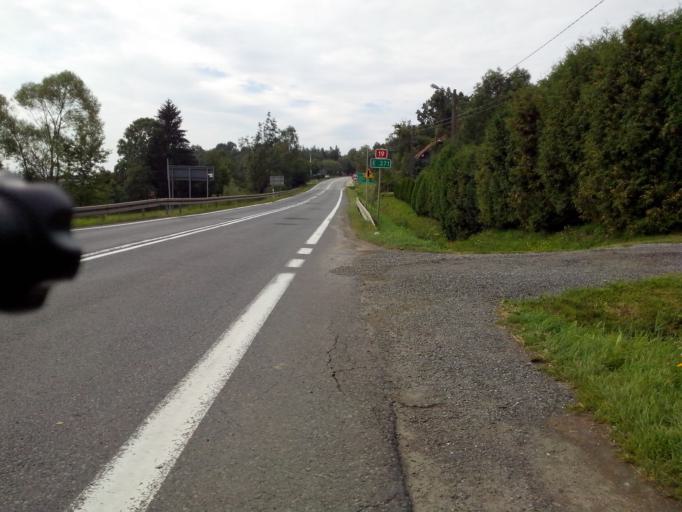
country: PL
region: Subcarpathian Voivodeship
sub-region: Powiat brzozowski
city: Domaradz
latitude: 49.7734
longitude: 21.9440
